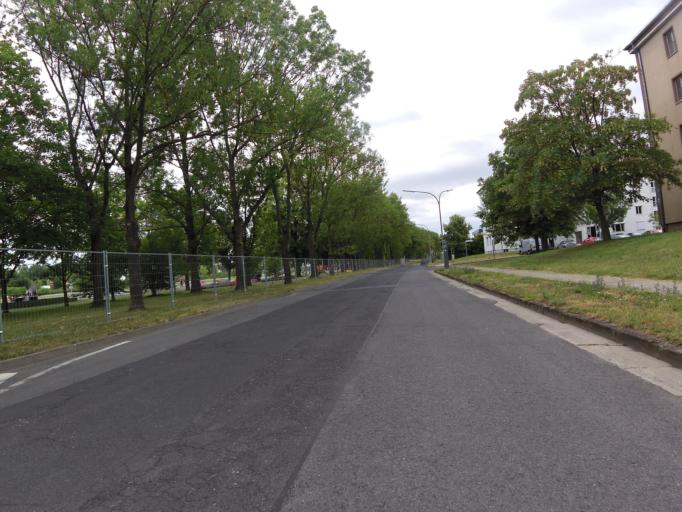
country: DE
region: Bavaria
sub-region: Regierungsbezirk Unterfranken
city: Gerbrunn
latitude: 49.7885
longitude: 9.9758
